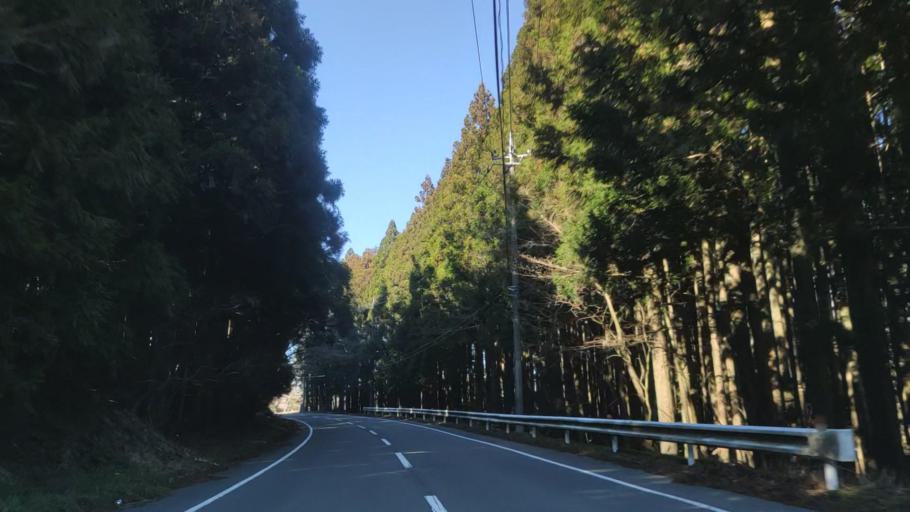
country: JP
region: Shizuoka
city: Fujinomiya
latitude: 35.3605
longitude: 138.6055
